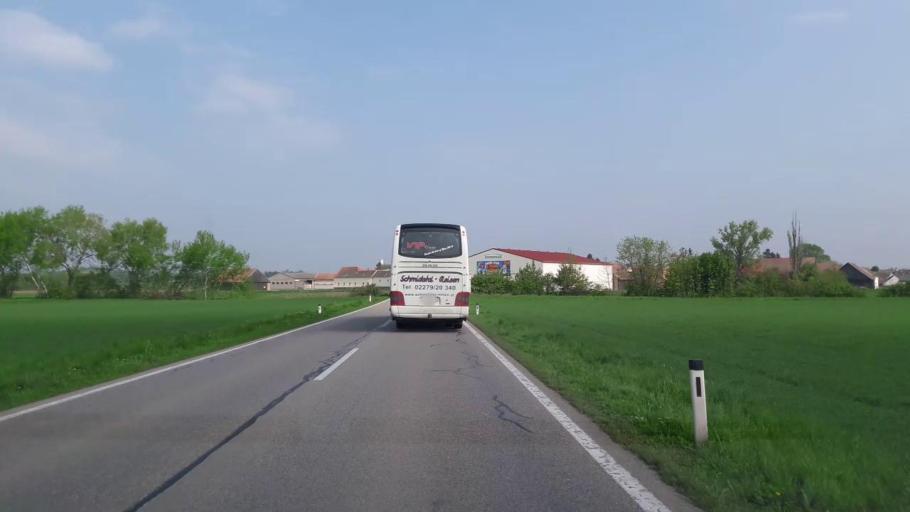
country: AT
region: Lower Austria
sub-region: Politischer Bezirk Hollabrunn
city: Guntersdorf
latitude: 48.6256
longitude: 16.0637
